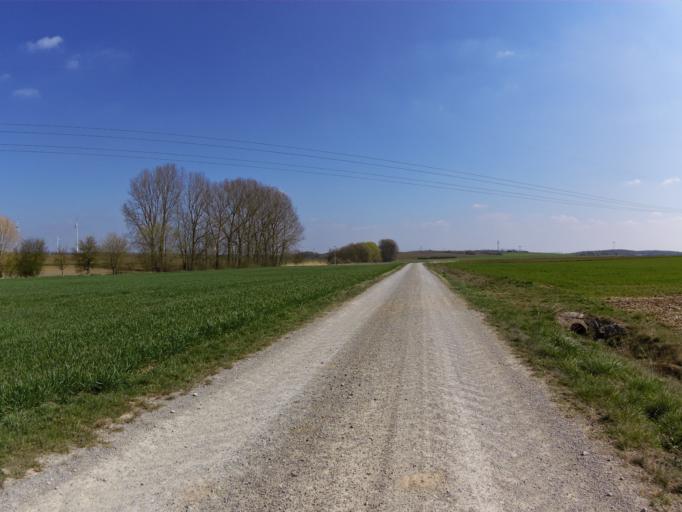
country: DE
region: Bavaria
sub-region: Regierungsbezirk Unterfranken
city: Biebelried
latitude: 49.7406
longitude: 10.0827
